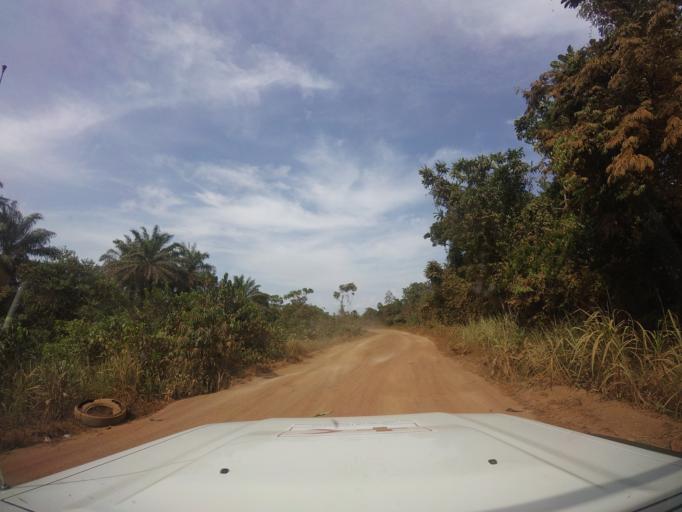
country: LR
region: Grand Cape Mount
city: Robertsport
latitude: 6.7026
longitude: -11.0903
